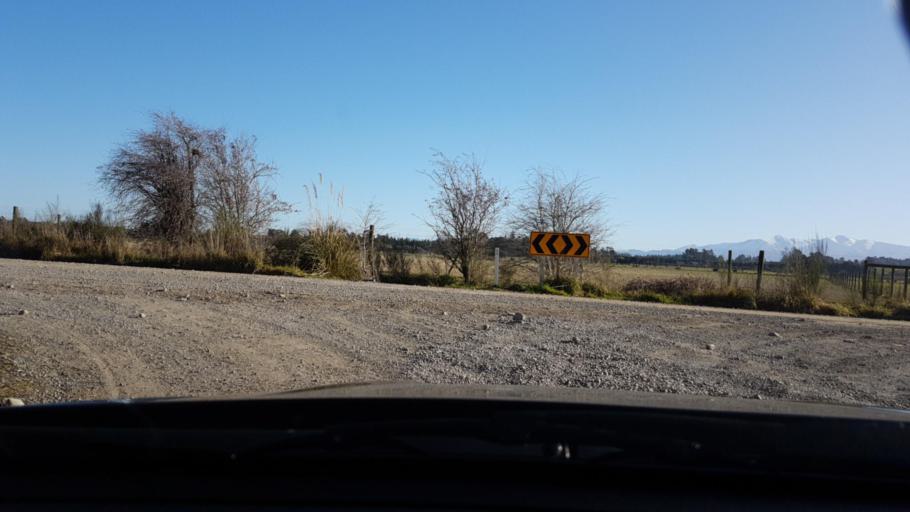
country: NZ
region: Canterbury
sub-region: Waimakariri District
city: Oxford
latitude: -43.2929
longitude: 172.1743
